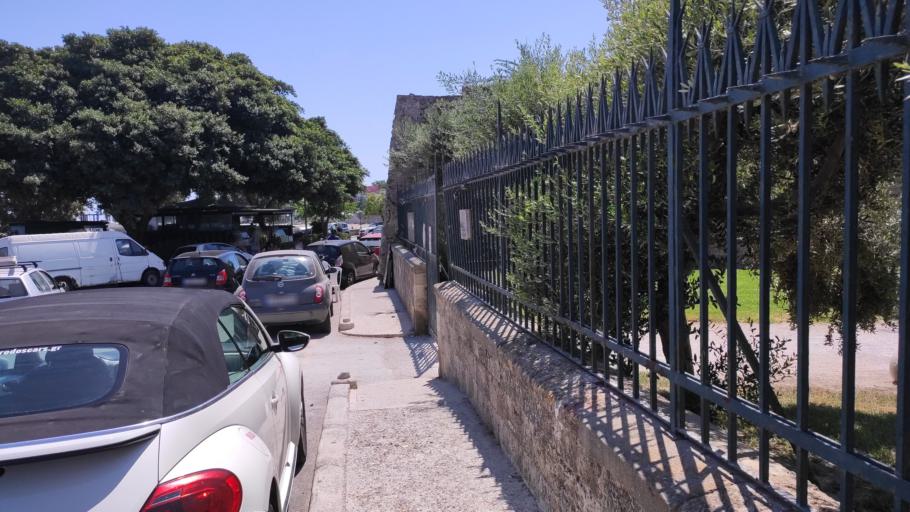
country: GR
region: South Aegean
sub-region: Nomos Dodekanisou
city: Rodos
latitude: 36.4417
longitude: 28.2328
